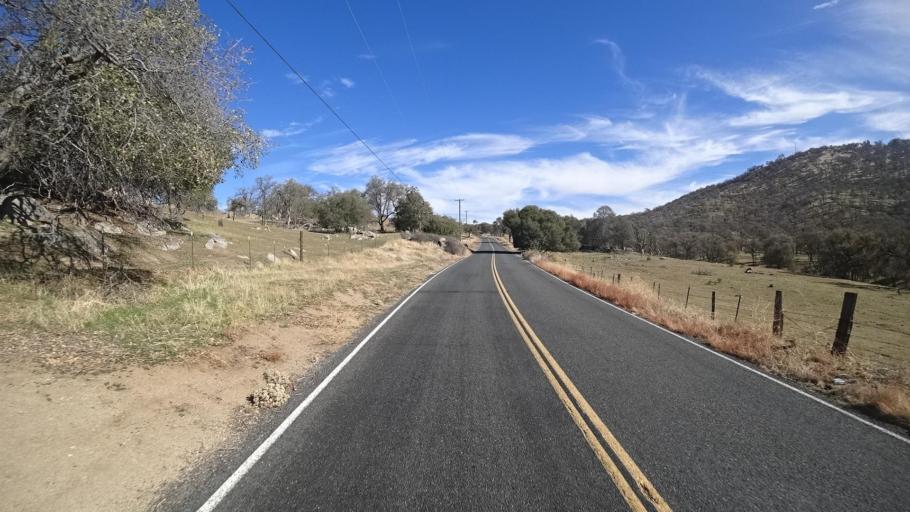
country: US
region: California
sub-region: Kern County
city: Alta Sierra
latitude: 35.6441
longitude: -118.7979
